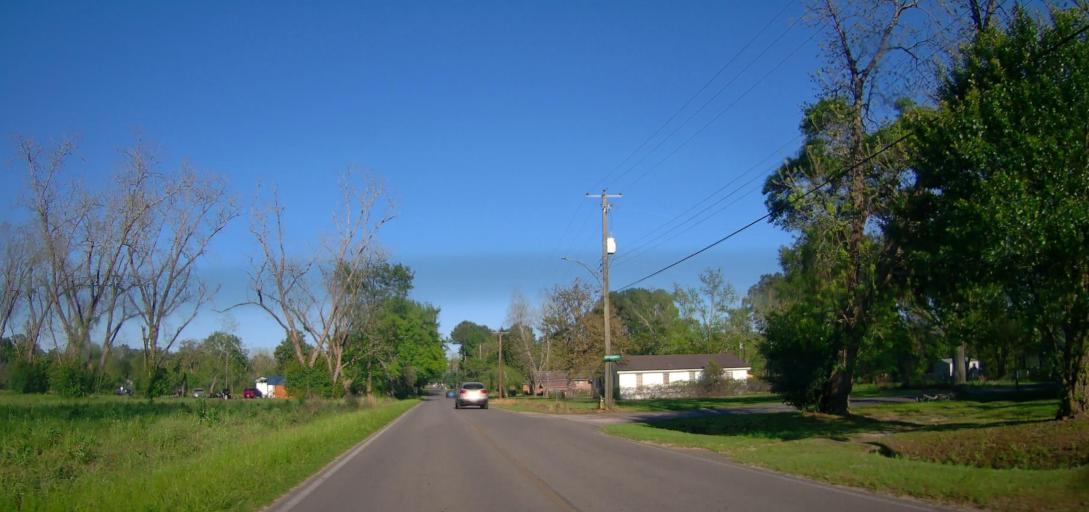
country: US
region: Georgia
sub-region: Ben Hill County
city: Fitzgerald
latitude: 31.7239
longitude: -83.2492
